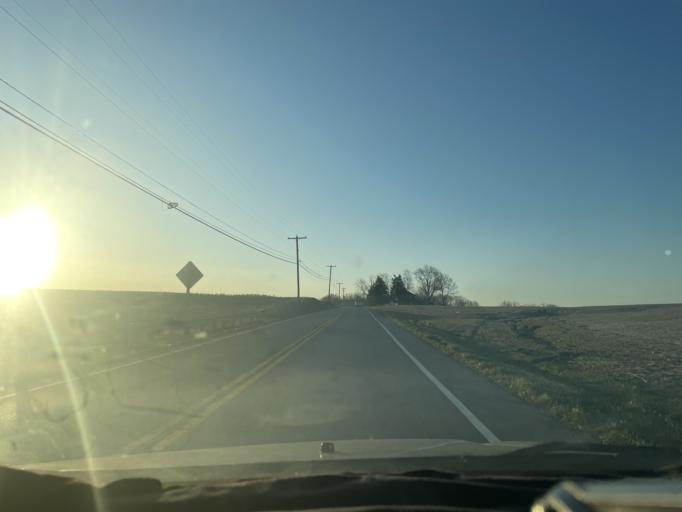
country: US
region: Maryland
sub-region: Frederick County
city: Adamstown
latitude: 39.2585
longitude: -77.4602
